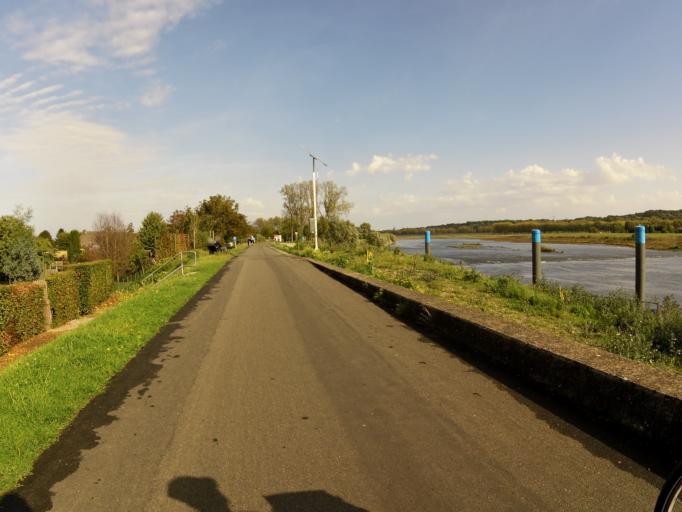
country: NL
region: Limburg
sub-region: Gemeente Stein
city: Elsloo
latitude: 50.9290
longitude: 5.7308
